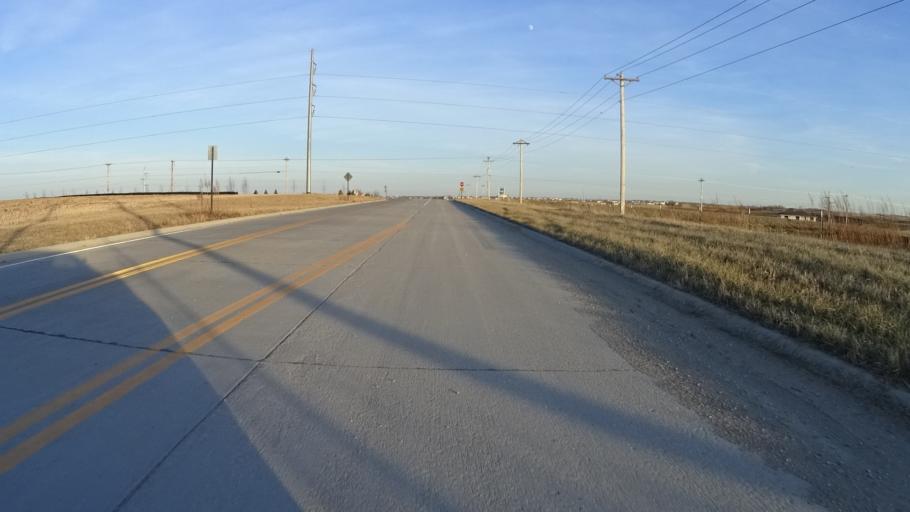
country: US
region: Nebraska
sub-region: Sarpy County
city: Papillion
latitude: 41.1326
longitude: -96.0923
